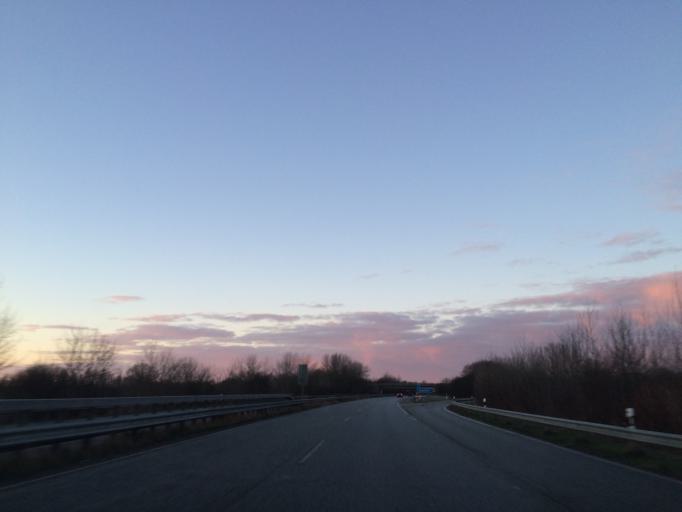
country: DE
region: Schleswig-Holstein
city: Altenkrempe
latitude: 54.1296
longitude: 10.8308
